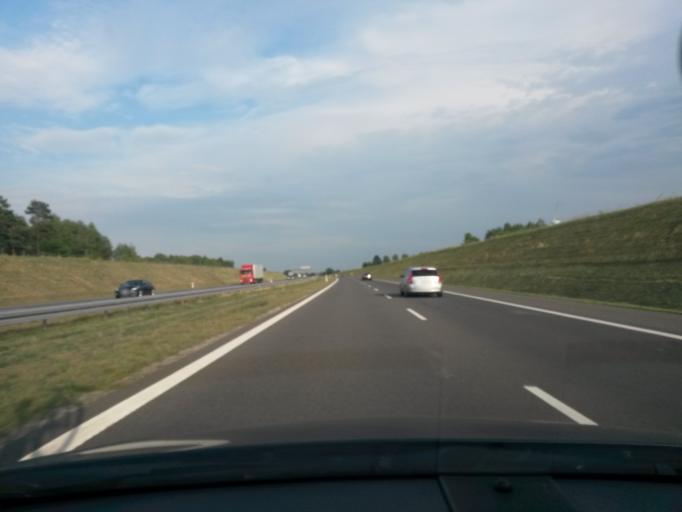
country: PL
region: Lodz Voivodeship
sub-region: Powiat zgierski
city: Zgierz
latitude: 51.9035
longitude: 19.4550
